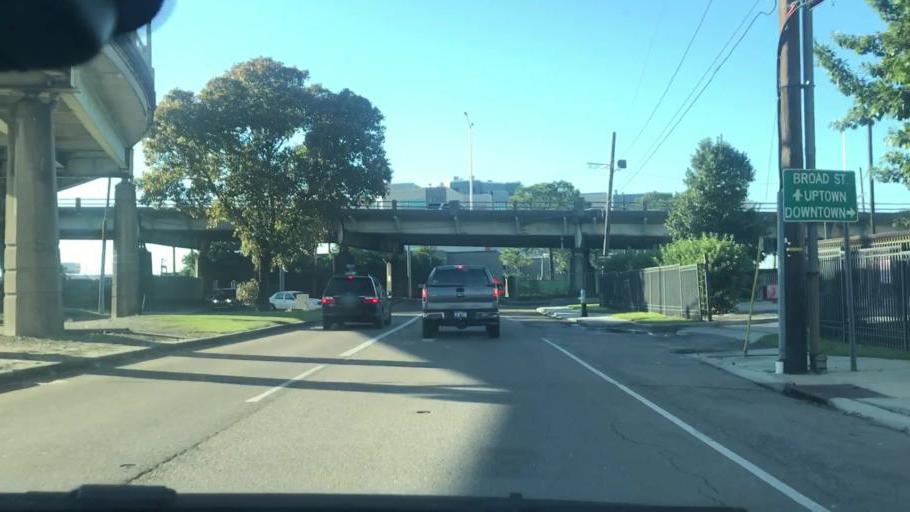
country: US
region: Louisiana
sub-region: Orleans Parish
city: New Orleans
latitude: 29.9587
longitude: -90.0926
